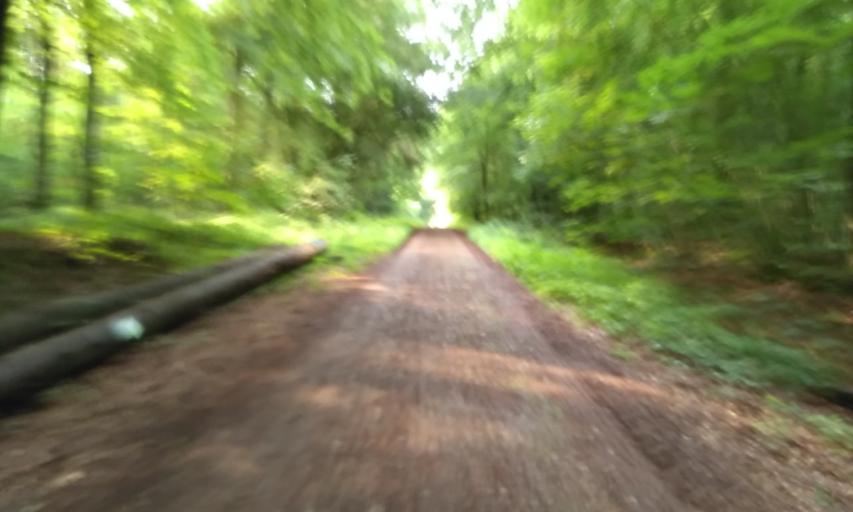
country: DE
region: Lower Saxony
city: Nottensdorf
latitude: 53.4756
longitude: 9.6205
